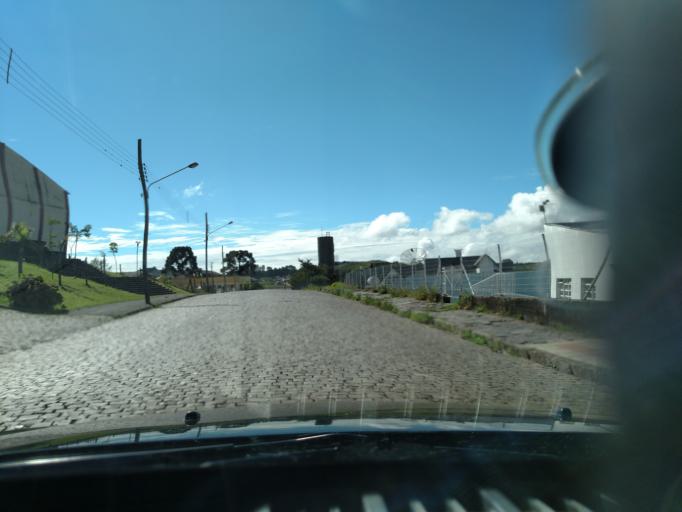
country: BR
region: Santa Catarina
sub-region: Sao Joaquim
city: Sao Joaquim
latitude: -28.2918
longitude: -49.9323
